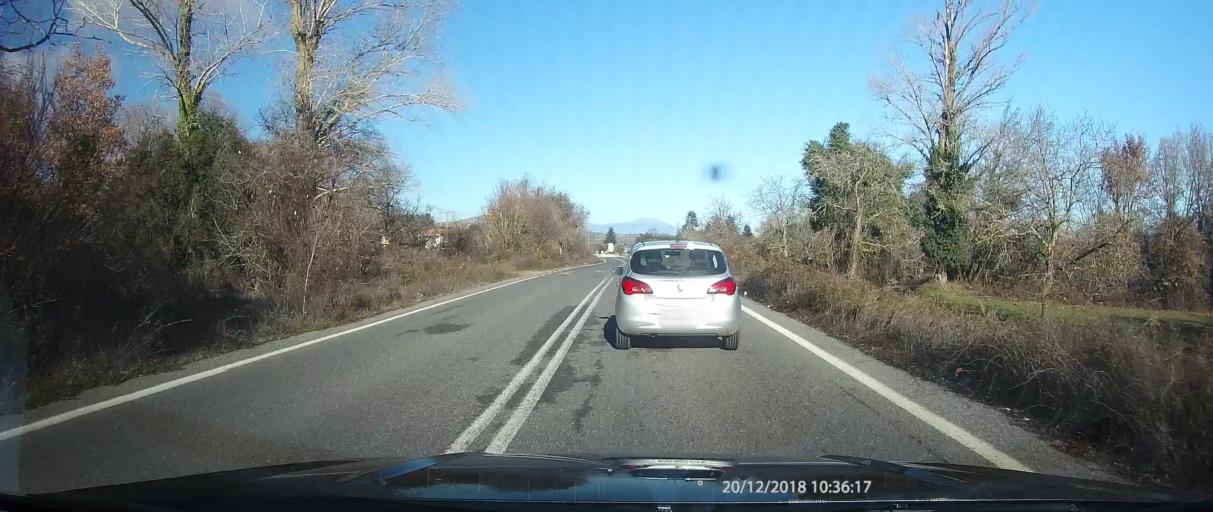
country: GR
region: Peloponnese
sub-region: Nomos Lakonias
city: Kariai
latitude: 37.3640
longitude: 22.4025
